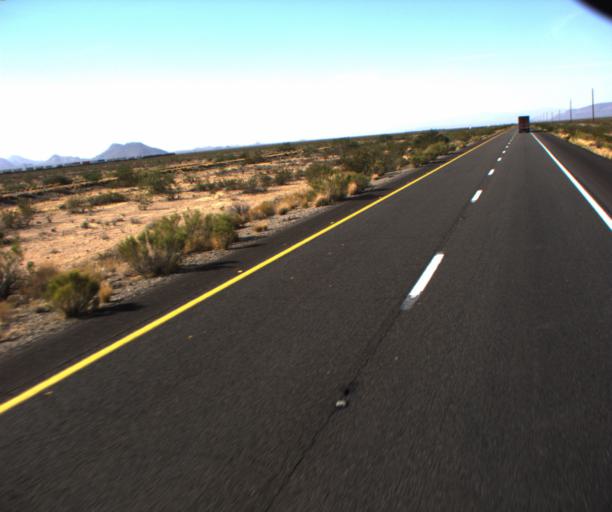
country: US
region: Arizona
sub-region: Mohave County
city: Kingman
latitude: 35.0170
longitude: -114.1339
